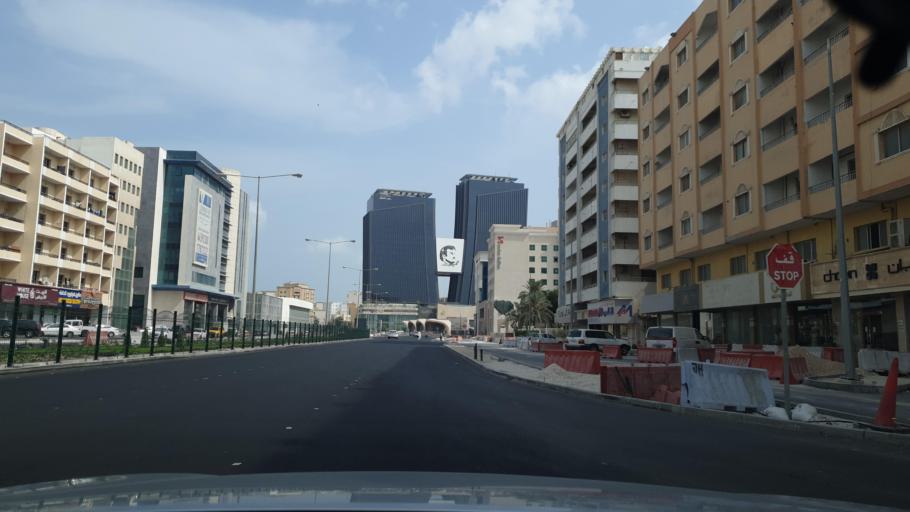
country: QA
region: Baladiyat ad Dawhah
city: Doha
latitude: 25.2810
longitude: 51.5027
